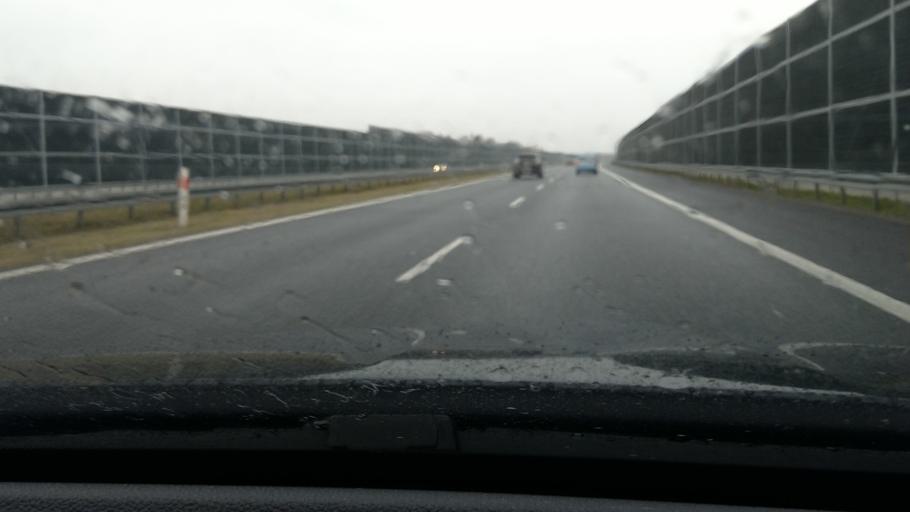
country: PL
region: Masovian Voivodeship
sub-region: Powiat zyrardowski
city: Guzow
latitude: 52.0733
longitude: 20.3052
